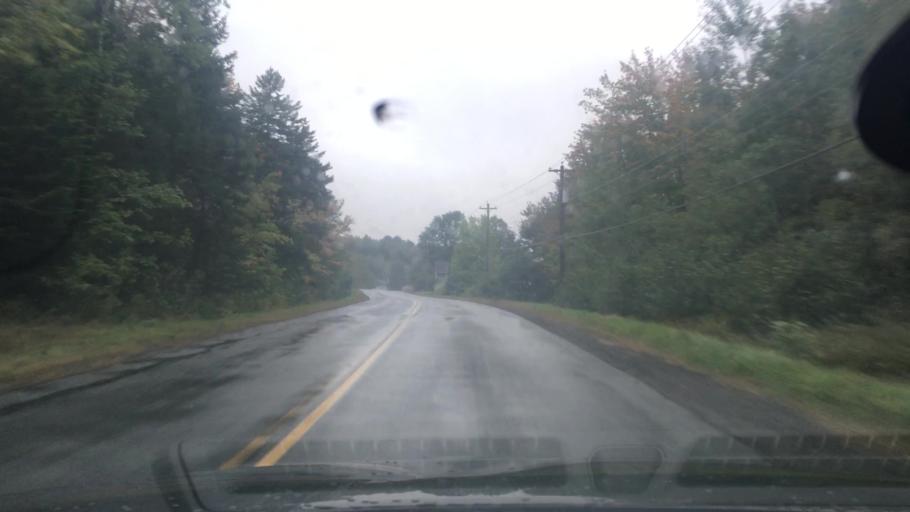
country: CA
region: Nova Scotia
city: Windsor
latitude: 44.8354
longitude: -64.2533
